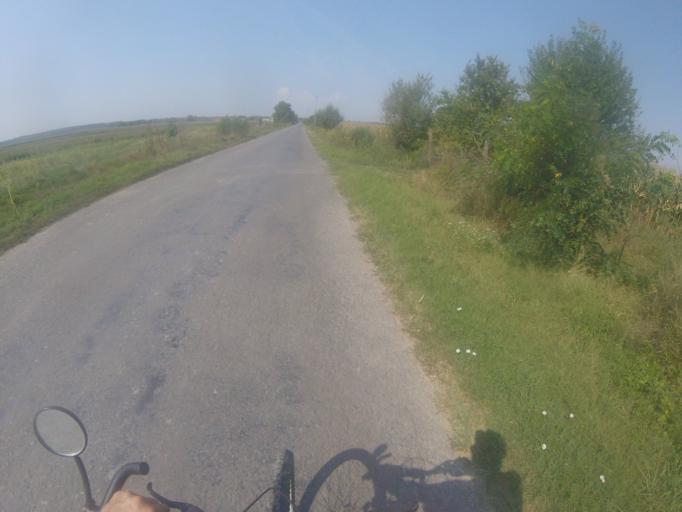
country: HU
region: Bacs-Kiskun
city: Ersekcsanad
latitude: 46.2562
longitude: 18.9442
